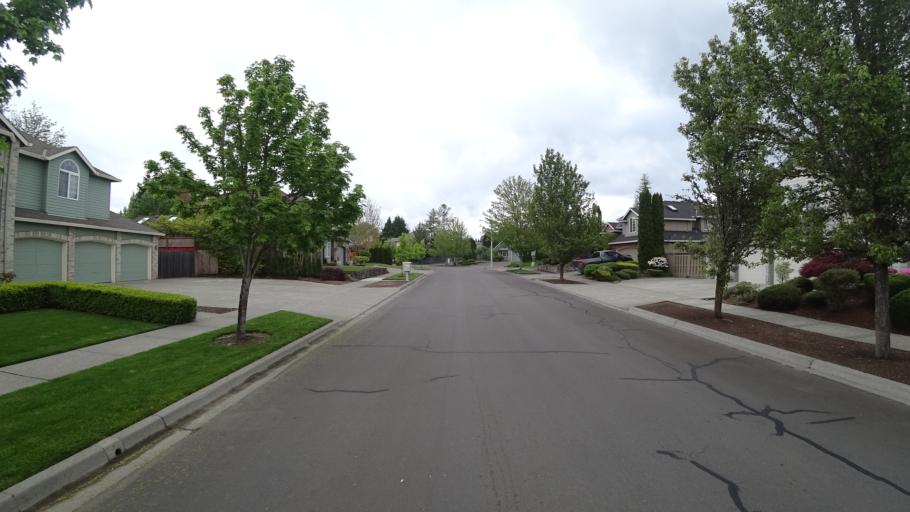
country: US
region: Oregon
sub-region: Washington County
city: Hillsboro
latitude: 45.5471
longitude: -122.9870
